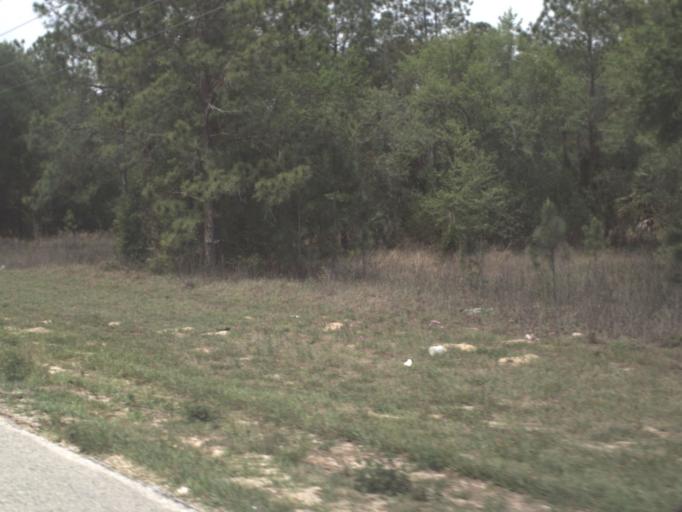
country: US
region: Florida
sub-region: Lake County
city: Mount Dora
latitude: 28.8515
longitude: -81.5960
